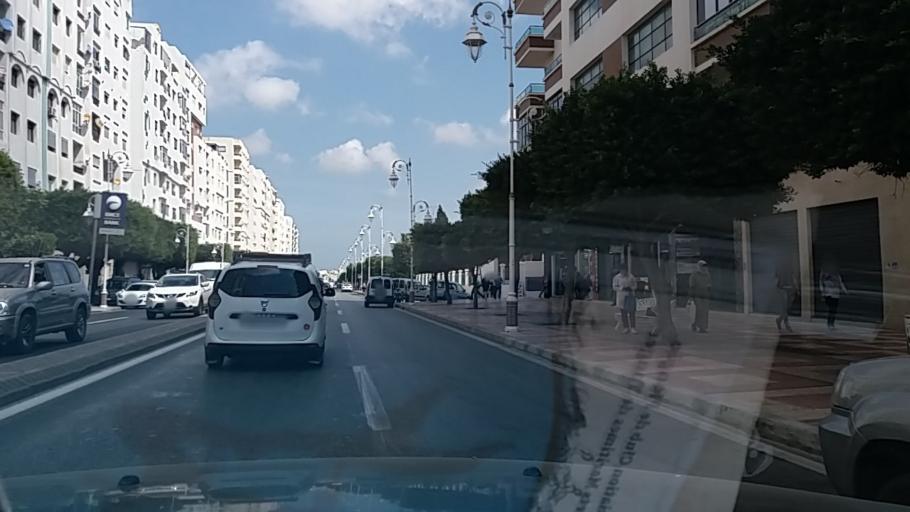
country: MA
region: Tanger-Tetouan
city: Tetouan
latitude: 35.5815
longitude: -5.3526
